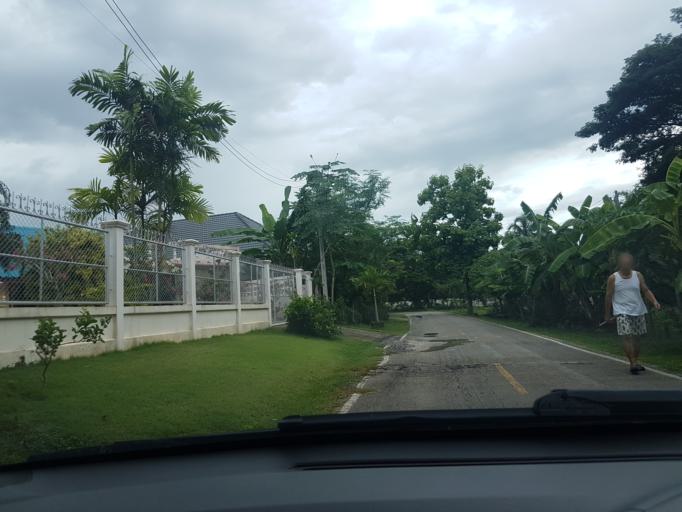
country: TH
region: Lampang
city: Lampang
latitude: 18.3099
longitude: 99.4786
